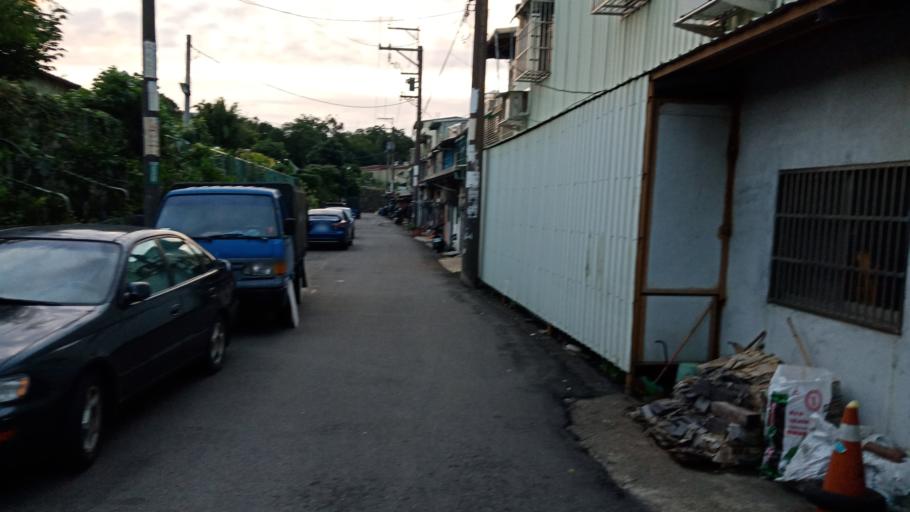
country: TW
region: Taiwan
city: Daxi
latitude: 24.8710
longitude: 121.1965
